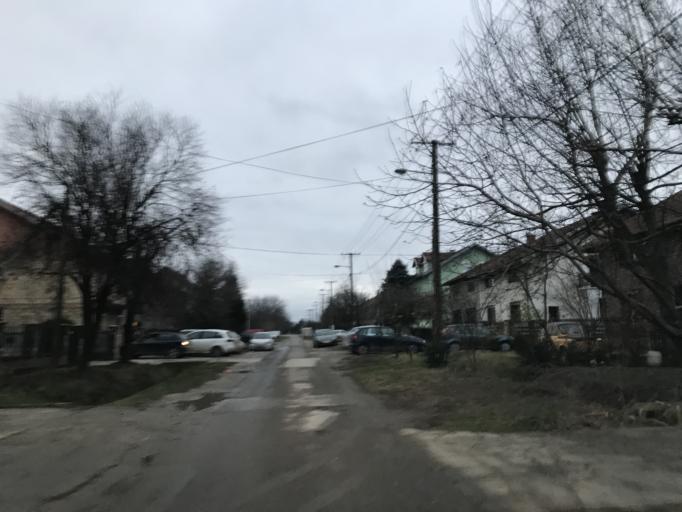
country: RS
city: Rumenka
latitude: 45.2974
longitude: 19.7347
